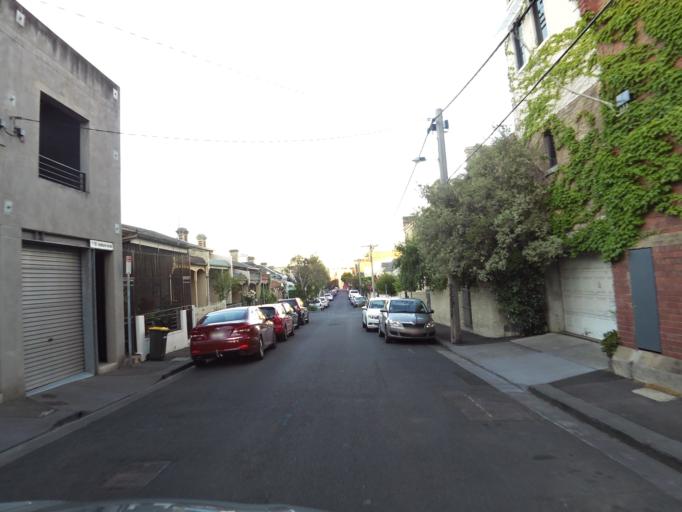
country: AU
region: Victoria
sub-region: Yarra
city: Richmond
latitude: -37.8207
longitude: 145.0004
